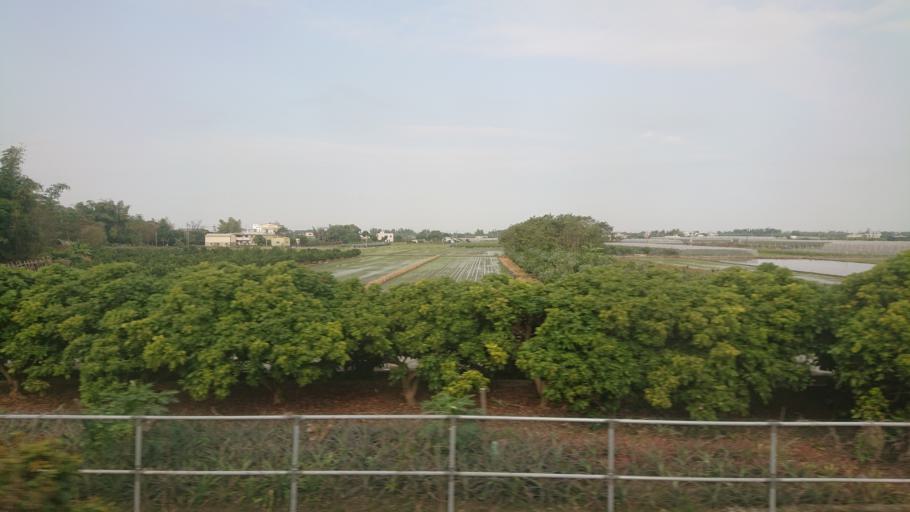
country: TW
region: Taiwan
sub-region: Yunlin
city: Douliu
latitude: 23.7287
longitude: 120.5767
